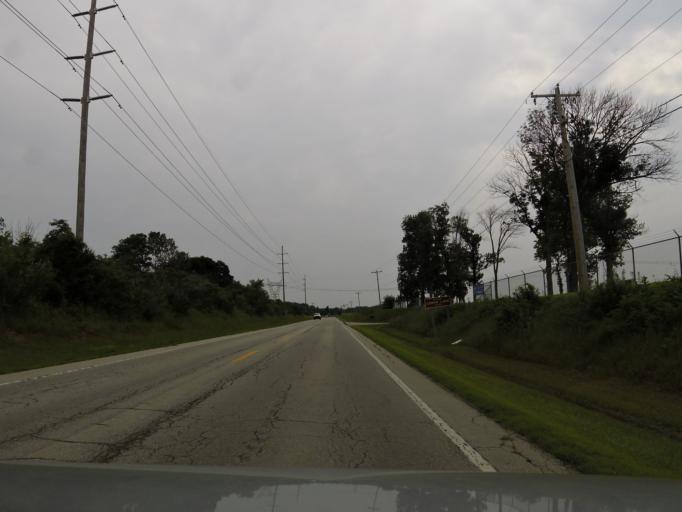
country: US
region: Ohio
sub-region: Clinton County
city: Wilmington
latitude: 39.4026
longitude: -83.8533
